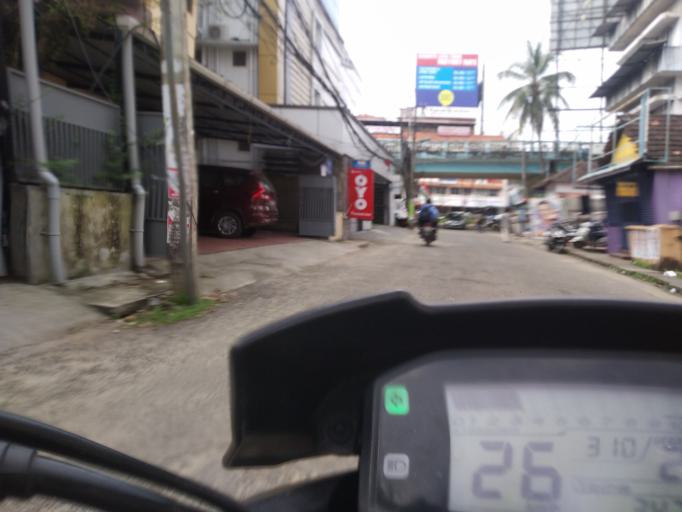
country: IN
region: Kerala
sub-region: Ernakulam
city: Cochin
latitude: 9.9645
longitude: 76.2918
